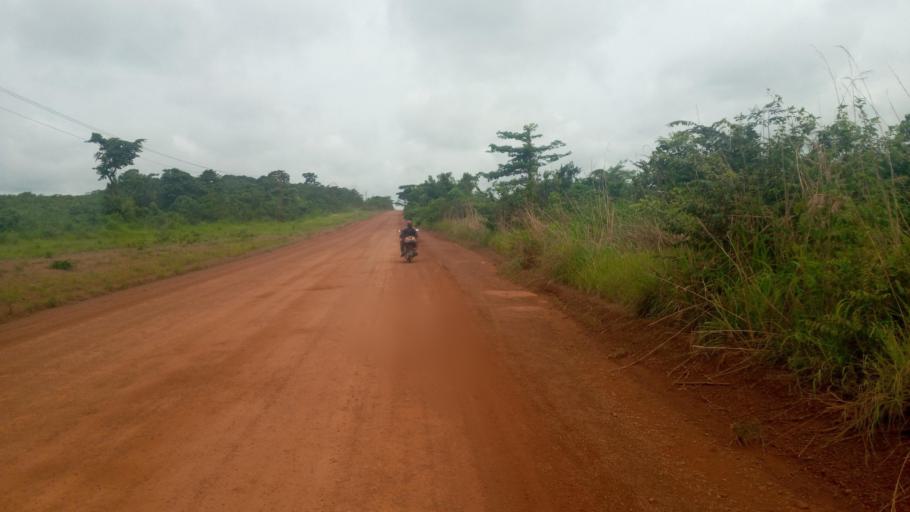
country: SL
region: Southern Province
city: Mogbwemo
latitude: 7.7383
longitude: -12.2816
